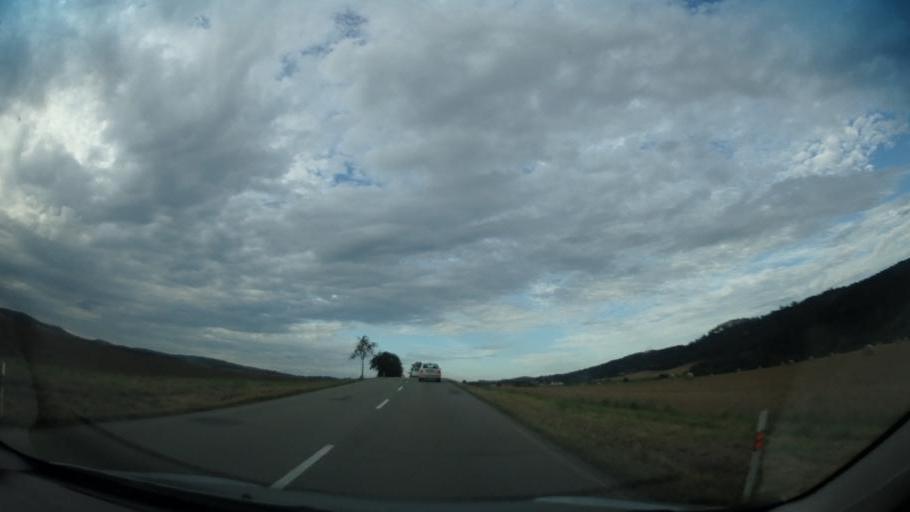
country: CZ
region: South Moravian
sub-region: Okres Blansko
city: Boskovice
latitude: 49.5186
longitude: 16.6803
